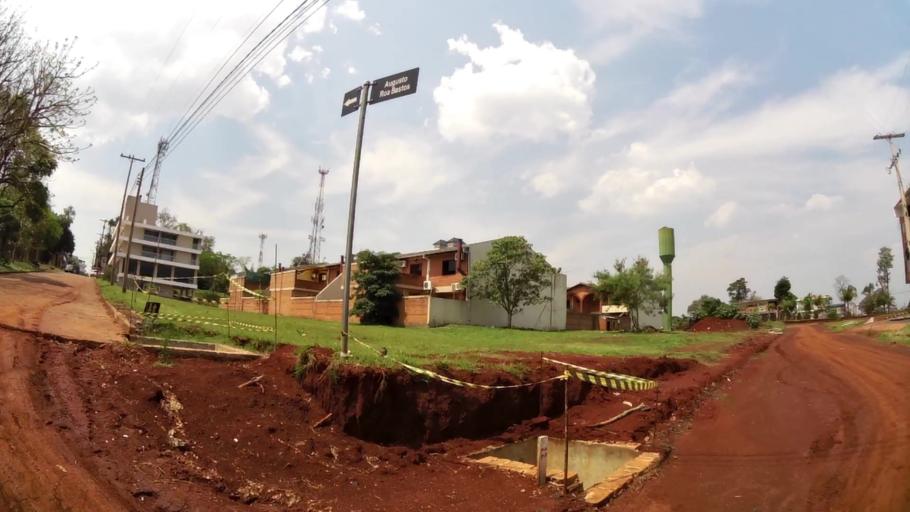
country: PY
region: Alto Parana
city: Ciudad del Este
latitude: -25.4835
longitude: -54.6251
